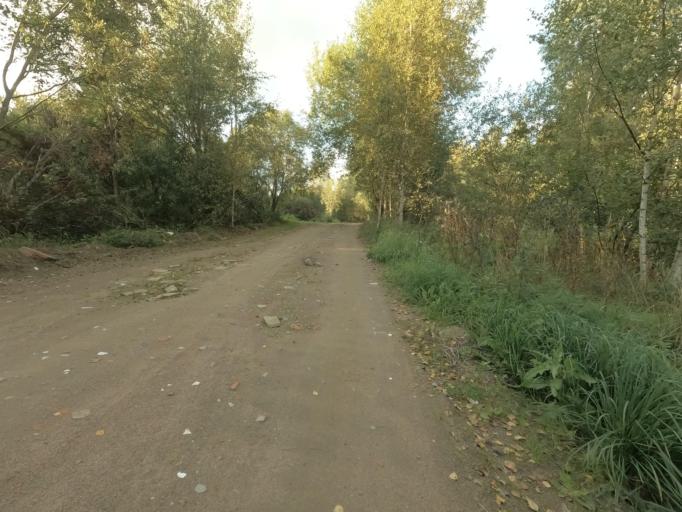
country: RU
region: Leningrad
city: Imeni Sverdlova
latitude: 59.8564
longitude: 30.7321
